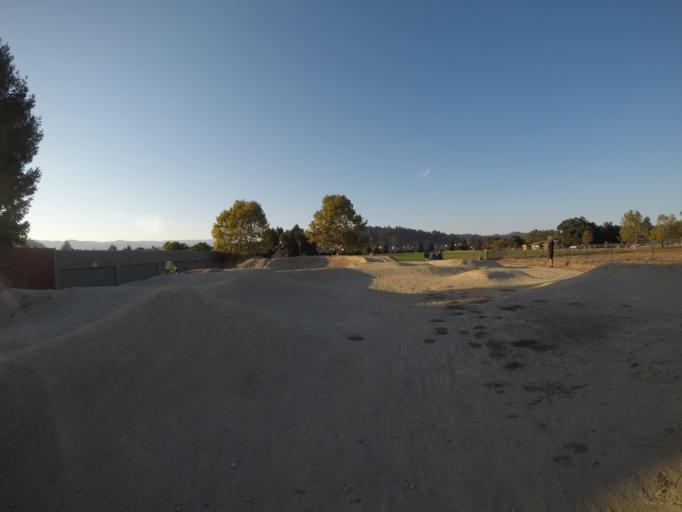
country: US
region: California
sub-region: Santa Cruz County
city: Scotts Valley
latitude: 37.0493
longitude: -122.0312
